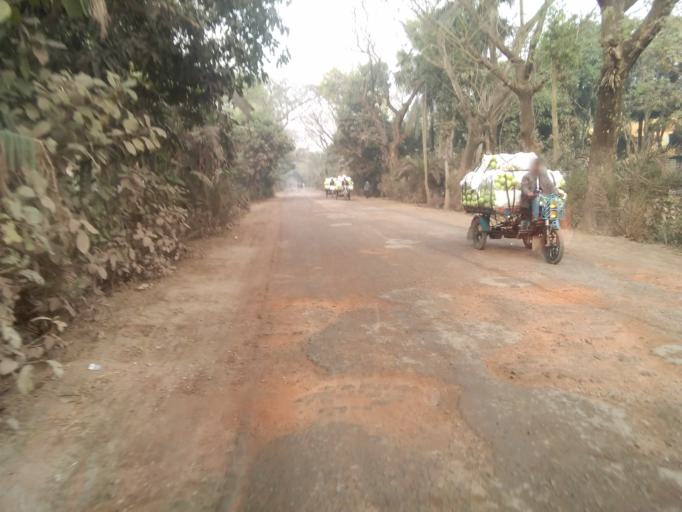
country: BD
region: Khulna
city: Satkhira
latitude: 22.6844
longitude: 89.0283
